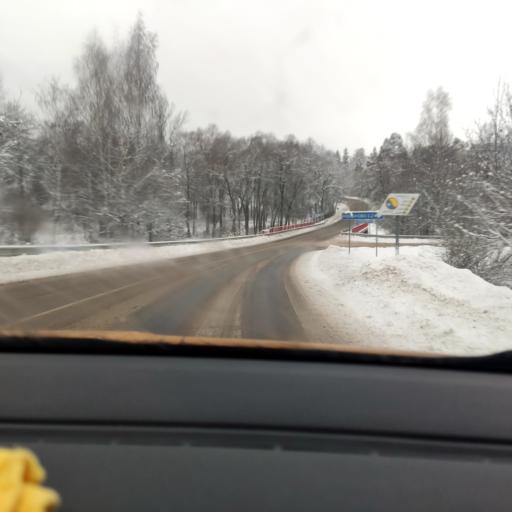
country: RU
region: Moskovskaya
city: Yershovo
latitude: 55.7718
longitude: 36.8012
